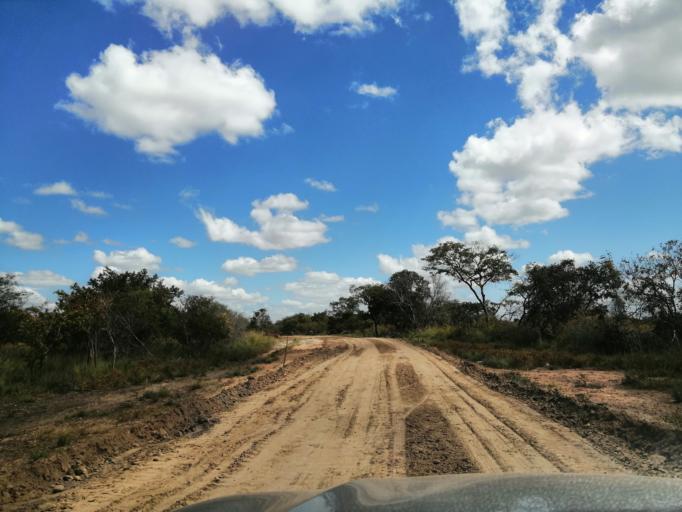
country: ZM
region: Central
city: Mumbwa
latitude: -14.5771
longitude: 27.2609
